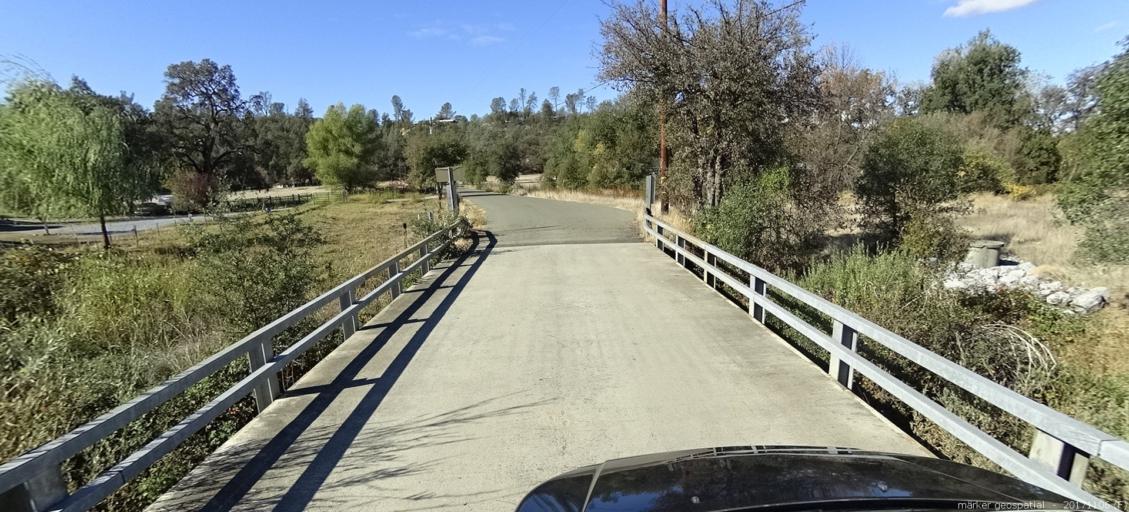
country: US
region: California
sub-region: Shasta County
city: Bella Vista
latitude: 40.6279
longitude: -122.2315
